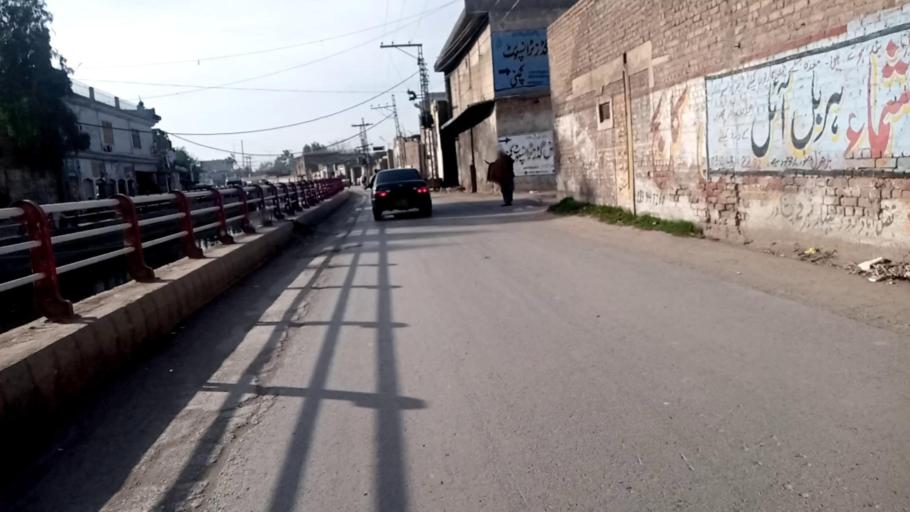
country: PK
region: Khyber Pakhtunkhwa
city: Peshawar
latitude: 34.0149
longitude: 71.6077
